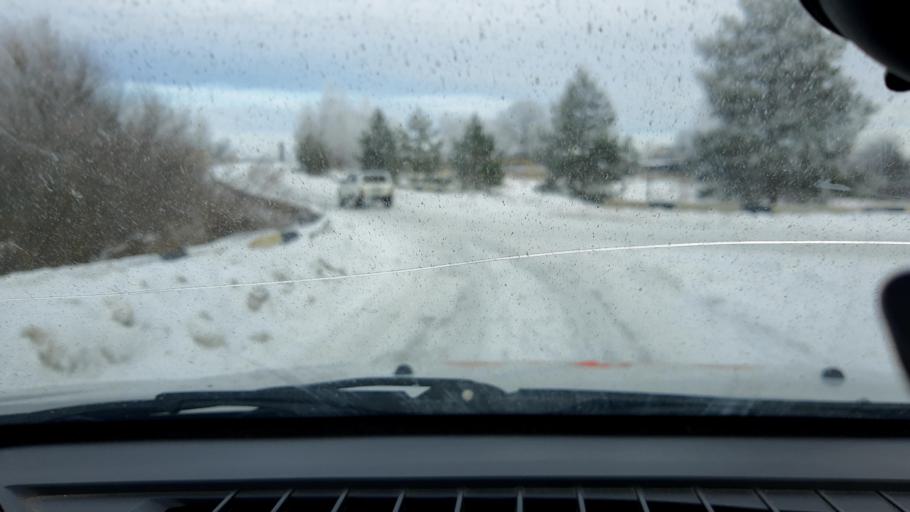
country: RU
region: Nizjnij Novgorod
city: Bogorodsk
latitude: 56.0429
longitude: 43.6290
